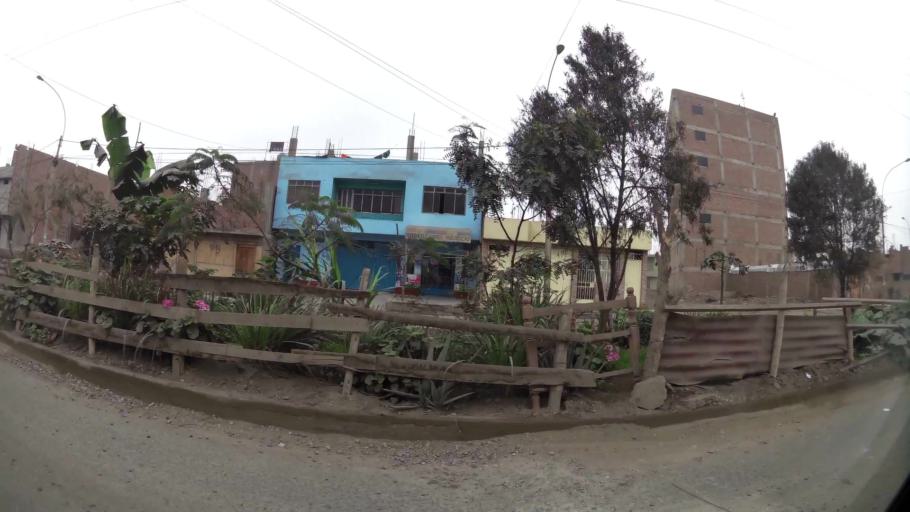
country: PE
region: Lima
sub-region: Lima
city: Urb. Santo Domingo
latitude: -11.8844
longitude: -77.0391
